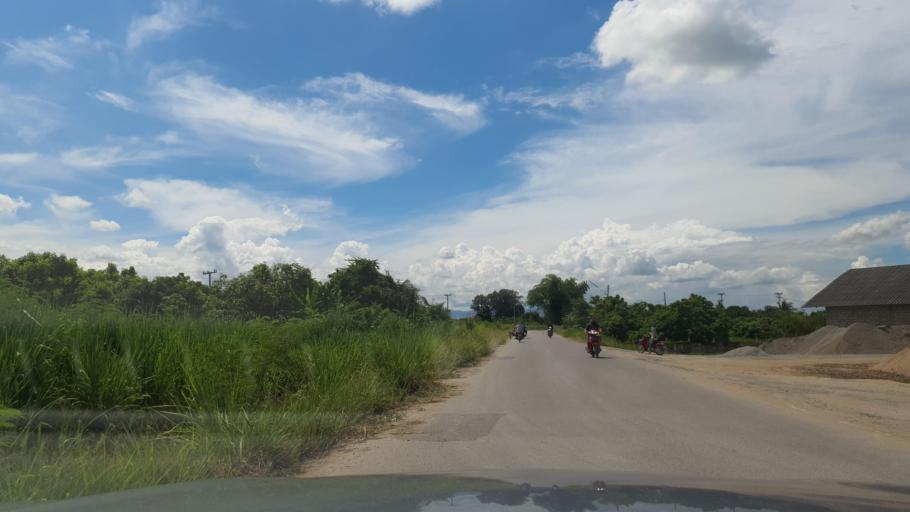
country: TH
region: Chiang Mai
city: San Pa Tong
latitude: 18.5833
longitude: 98.9075
